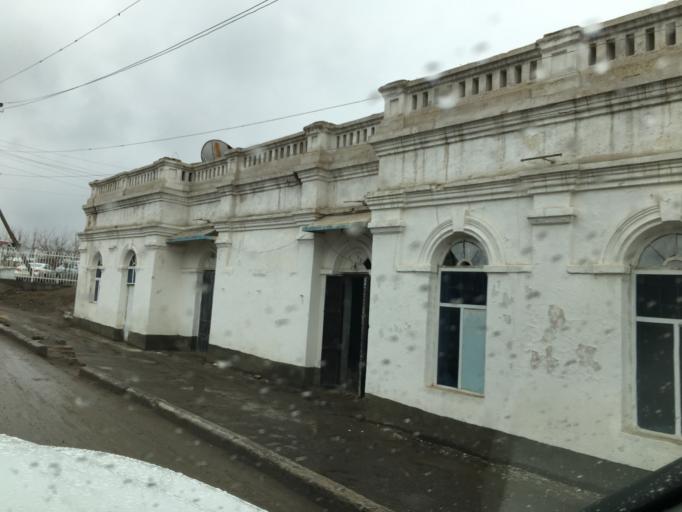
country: TM
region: Mary
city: Yoloeten
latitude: 37.2929
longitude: 62.3596
